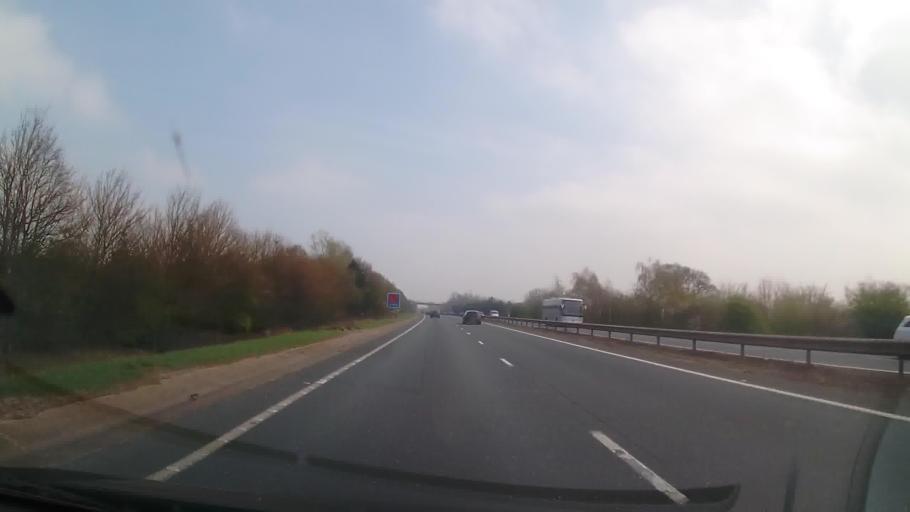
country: GB
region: England
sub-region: Derbyshire
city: Etwall
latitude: 52.8795
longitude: -1.6636
